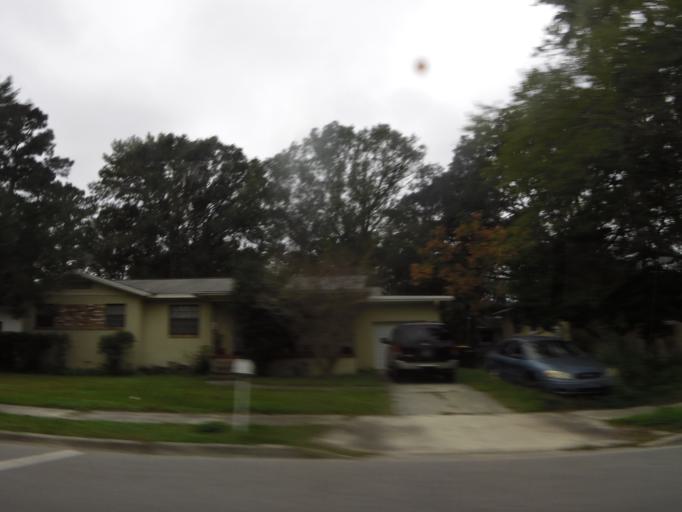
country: US
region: Florida
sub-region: Clay County
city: Bellair-Meadowbrook Terrace
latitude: 30.2567
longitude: -81.7472
